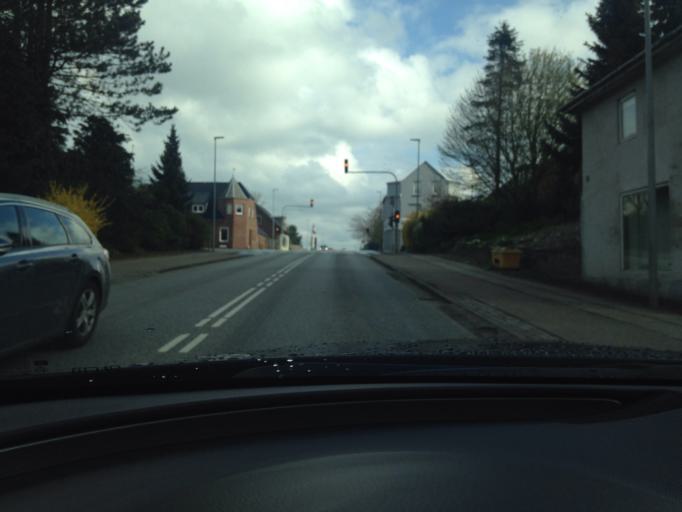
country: DK
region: South Denmark
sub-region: Kolding Kommune
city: Kolding
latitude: 55.5240
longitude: 9.4631
